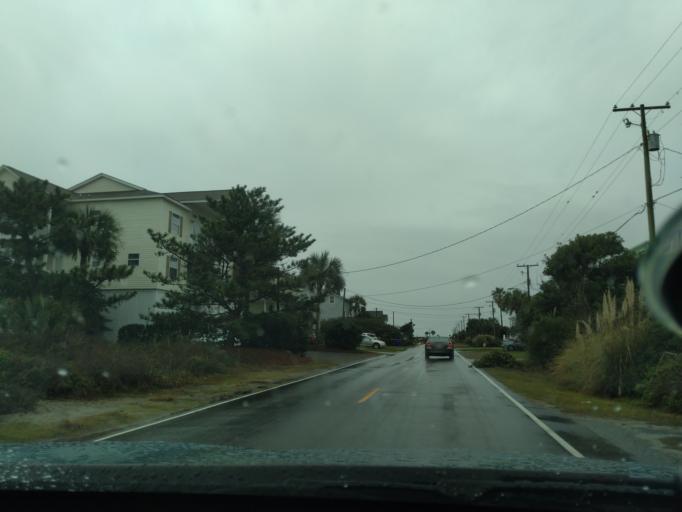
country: US
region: South Carolina
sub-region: Charleston County
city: Folly Beach
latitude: 32.6719
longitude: -79.9046
